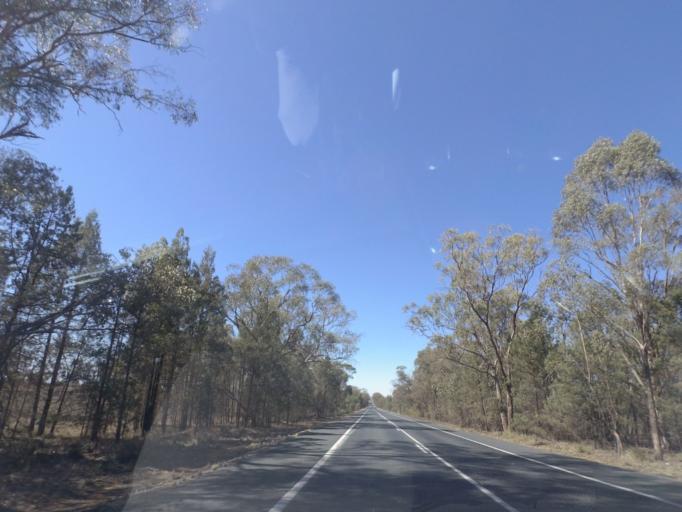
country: AU
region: New South Wales
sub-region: Bland
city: West Wyalong
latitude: -34.1687
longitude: 147.1154
